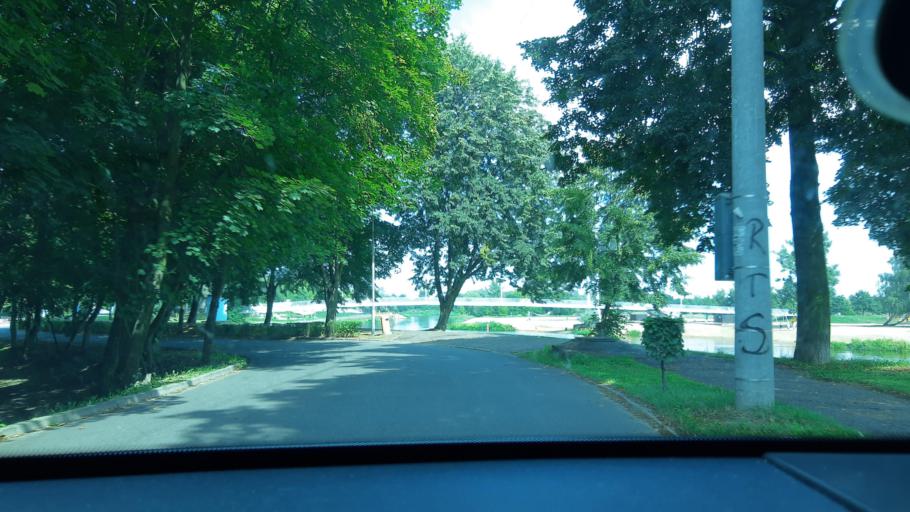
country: PL
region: Lodz Voivodeship
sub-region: Powiat sieradzki
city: Sieradz
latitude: 51.5992
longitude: 18.7424
